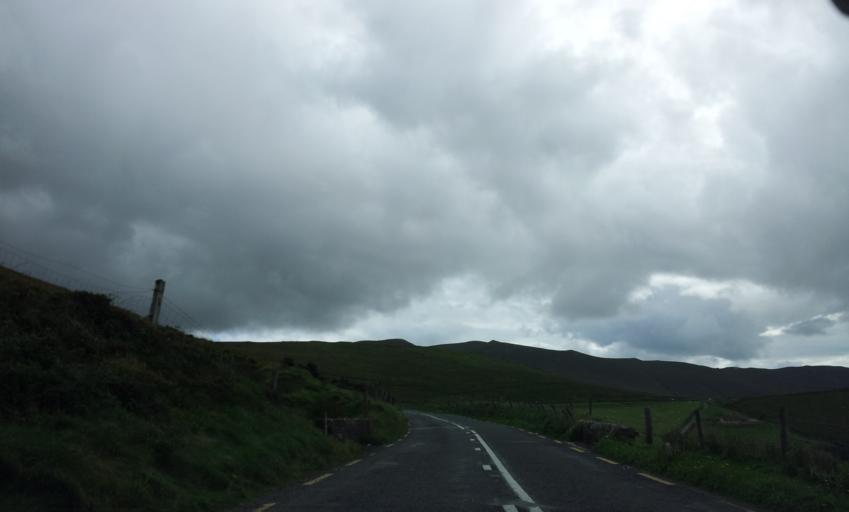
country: IE
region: Munster
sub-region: Ciarrai
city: Killorglin
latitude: 52.2047
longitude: -9.9301
